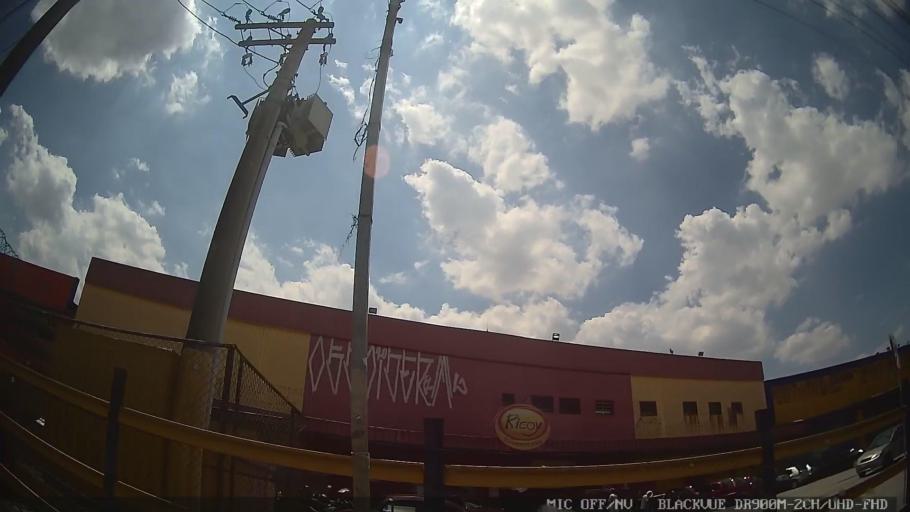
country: BR
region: Sao Paulo
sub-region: Taboao Da Serra
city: Taboao da Serra
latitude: -23.6625
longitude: -46.7805
